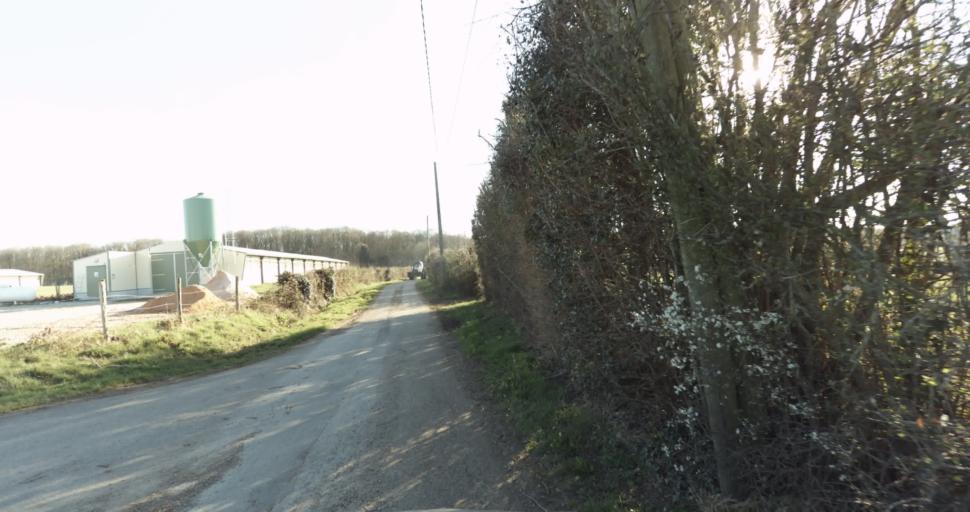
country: FR
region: Lower Normandy
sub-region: Departement du Calvados
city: Livarot
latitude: 48.9798
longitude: 0.0851
